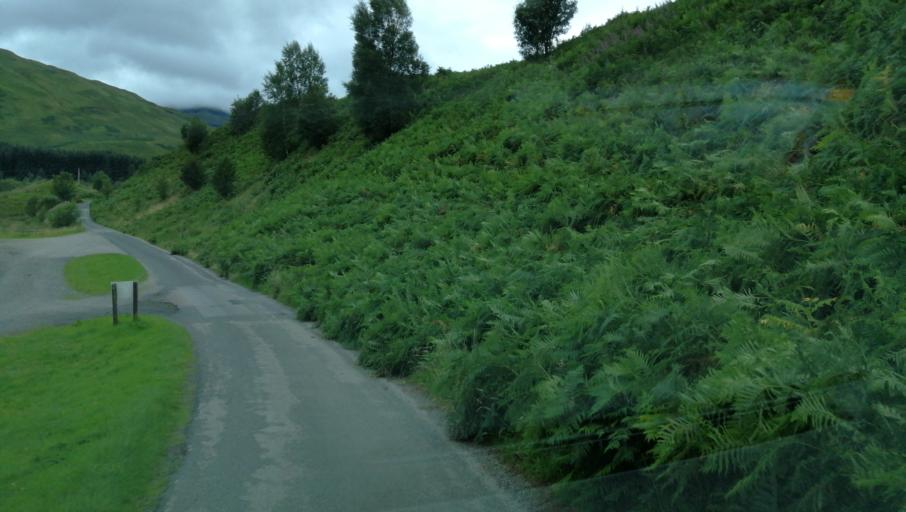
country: GB
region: Scotland
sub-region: Argyll and Bute
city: Garelochhead
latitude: 56.4246
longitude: -4.6719
